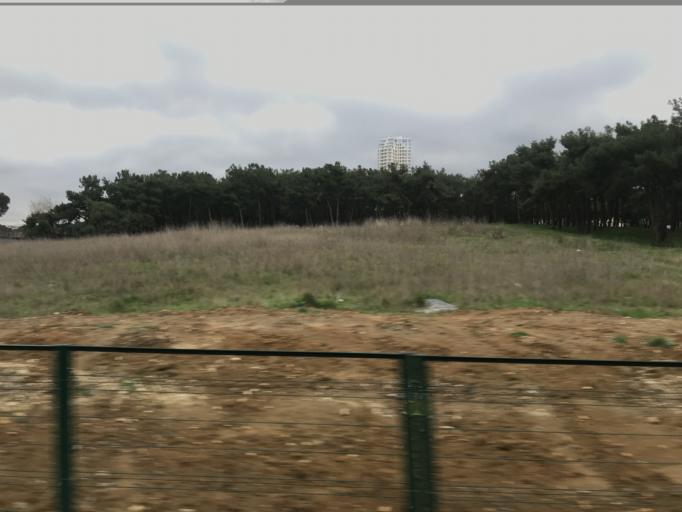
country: TR
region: Istanbul
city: Pendik
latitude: 40.8825
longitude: 29.2151
